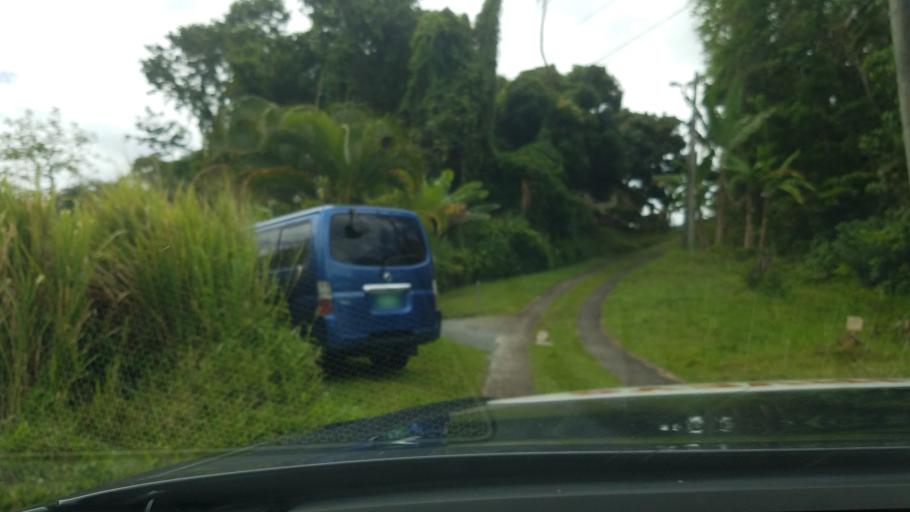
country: LC
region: Castries Quarter
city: Bisee
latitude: 14.0026
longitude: -60.9726
